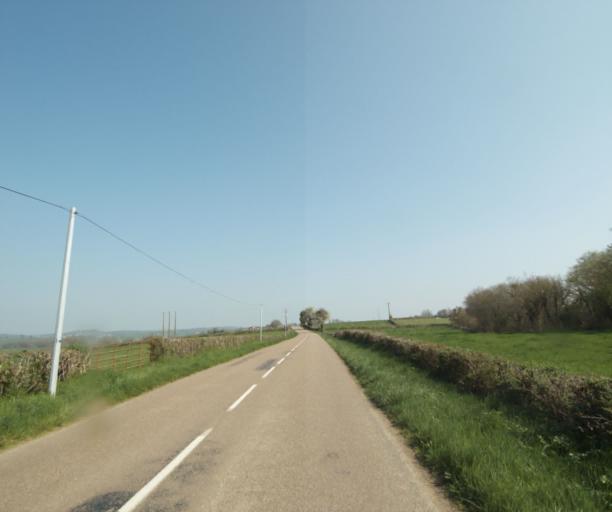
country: FR
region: Bourgogne
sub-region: Departement de Saone-et-Loire
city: Charolles
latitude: 46.4863
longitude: 4.3444
